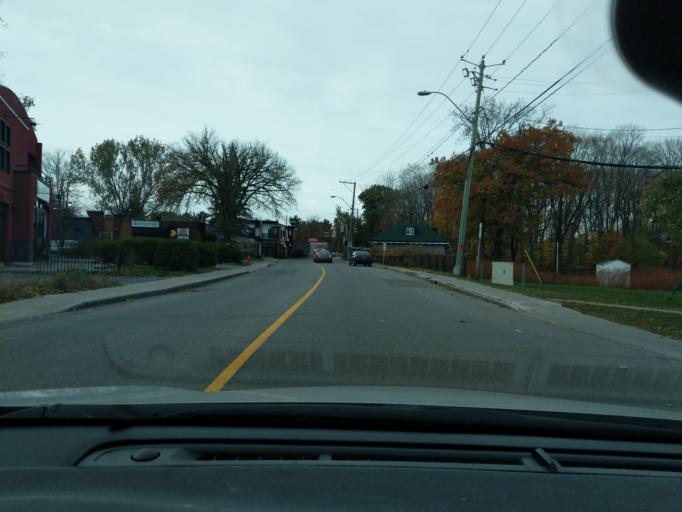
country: CA
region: Quebec
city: Quebec
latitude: 46.7847
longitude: -71.2462
